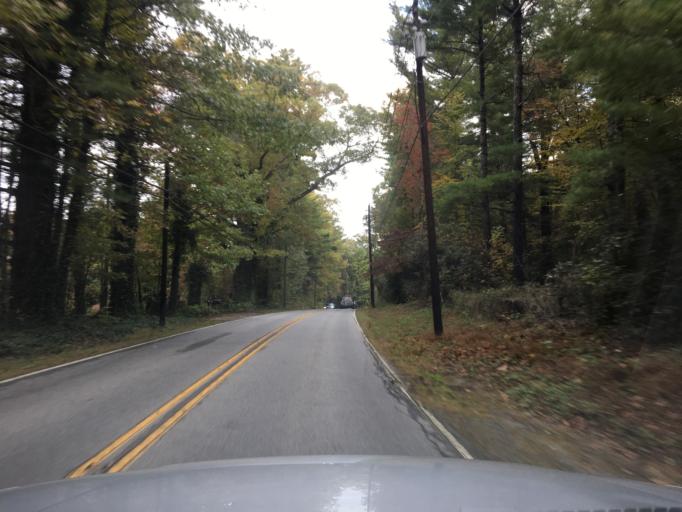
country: US
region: North Carolina
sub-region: Henderson County
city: Flat Rock
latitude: 35.2645
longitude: -82.4395
